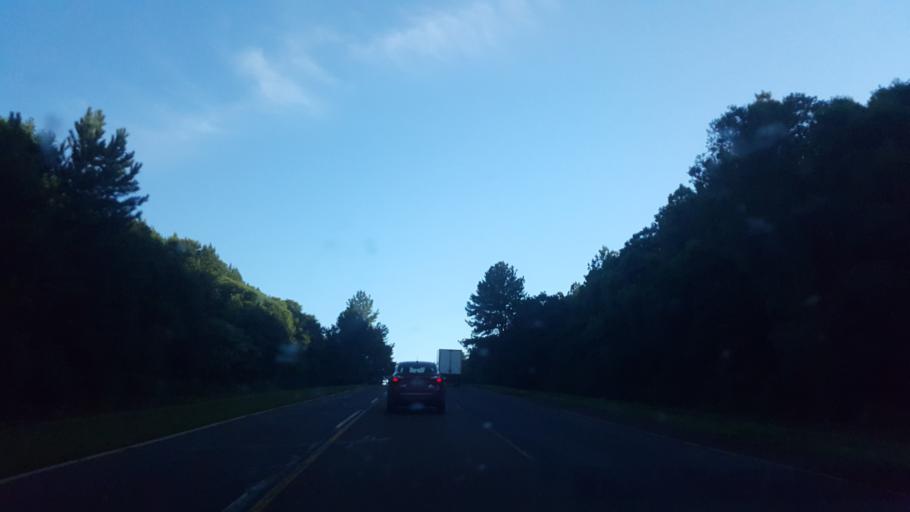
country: AR
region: Misiones
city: Garuhape
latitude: -26.7683
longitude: -54.8906
